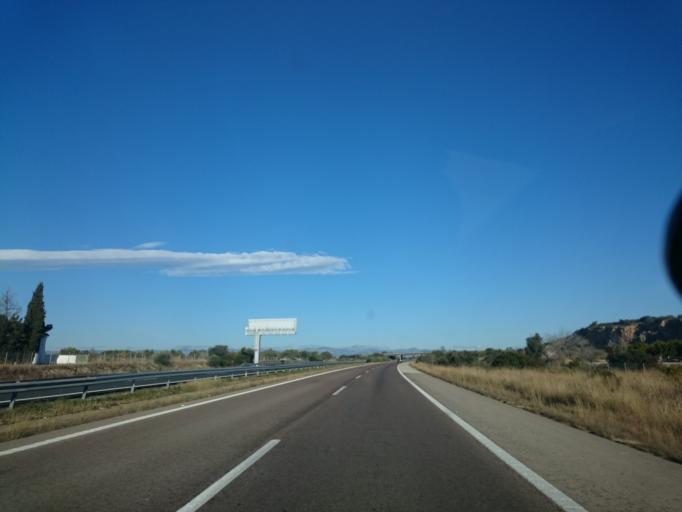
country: ES
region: Valencia
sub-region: Provincia de Castello
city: Vinaros
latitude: 40.4867
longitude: 0.4159
